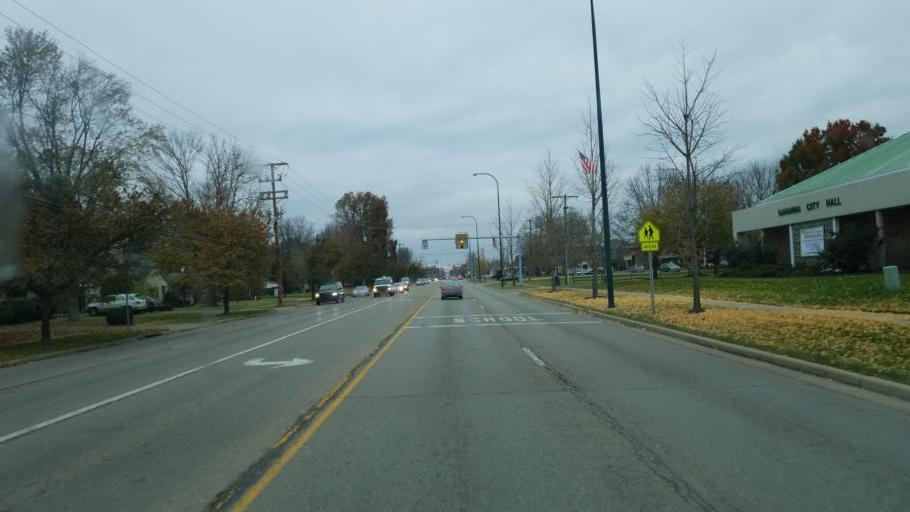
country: US
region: Ohio
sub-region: Franklin County
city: Gahanna
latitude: 40.0140
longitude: -82.8669
